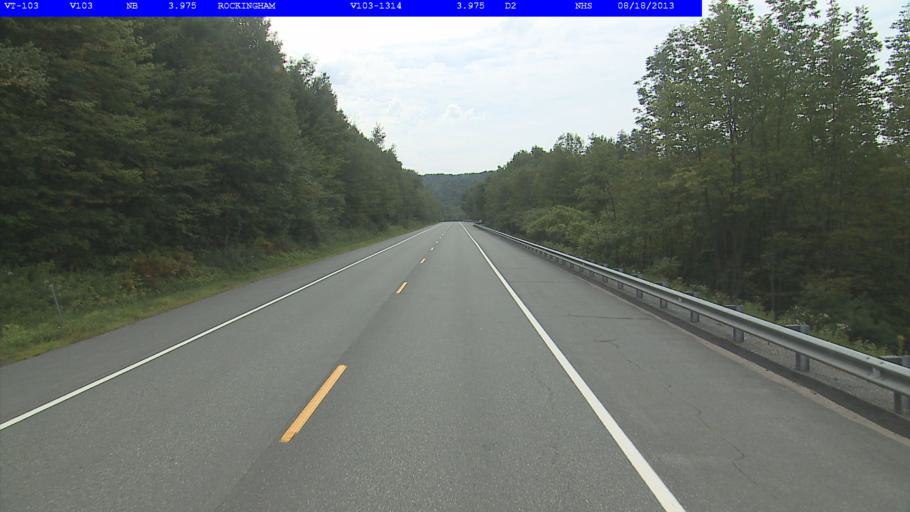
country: US
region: Vermont
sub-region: Windham County
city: Rockingham
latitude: 43.2048
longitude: -72.5265
